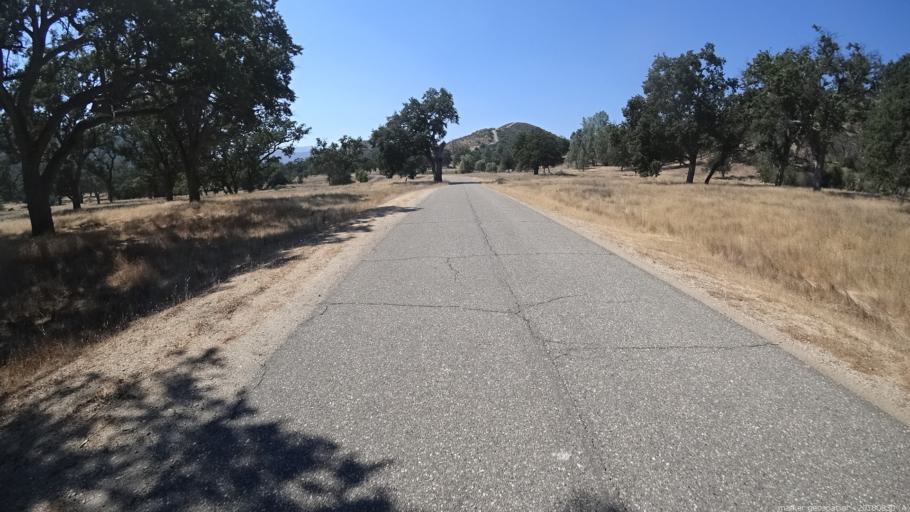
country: US
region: California
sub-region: Monterey County
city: King City
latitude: 36.0735
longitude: -121.3442
